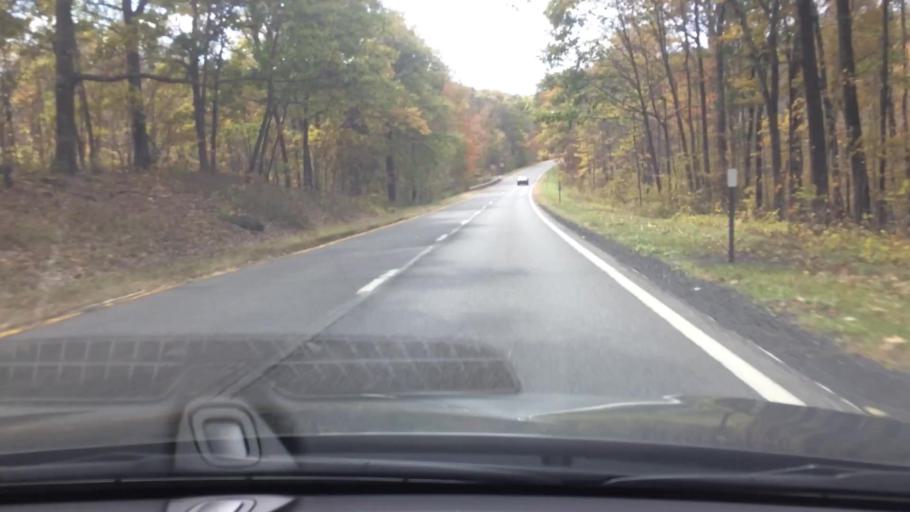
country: US
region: New York
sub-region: Dutchess County
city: Pine Plains
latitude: 41.9408
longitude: -73.7539
